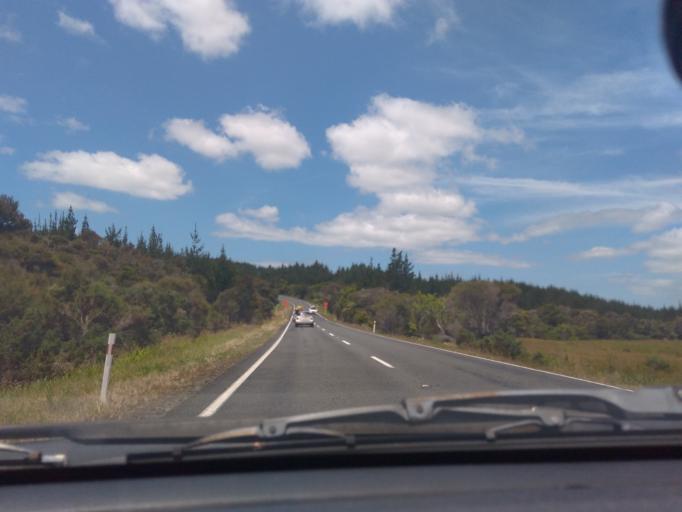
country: NZ
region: Northland
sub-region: Far North District
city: Kerikeri
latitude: -35.1224
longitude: 173.8447
